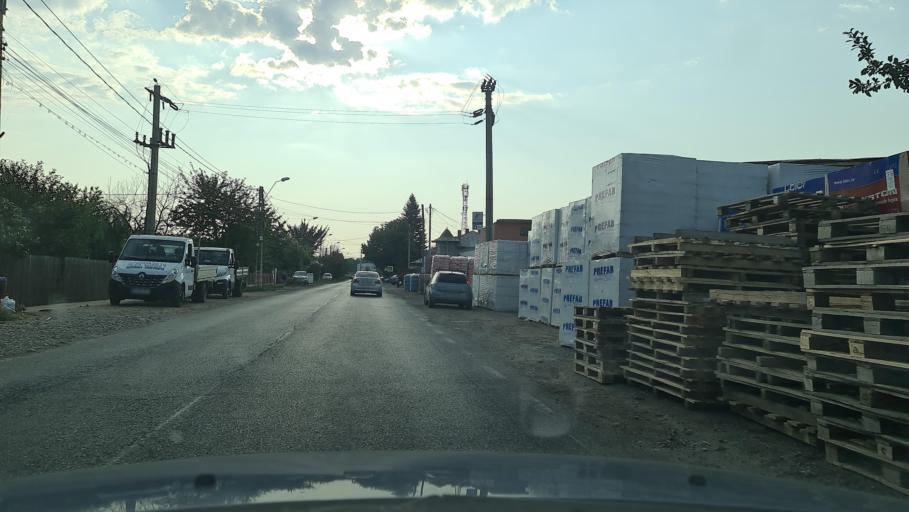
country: RO
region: Calarasi
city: Lehliu-Gara
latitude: 44.4388
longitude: 26.8591
